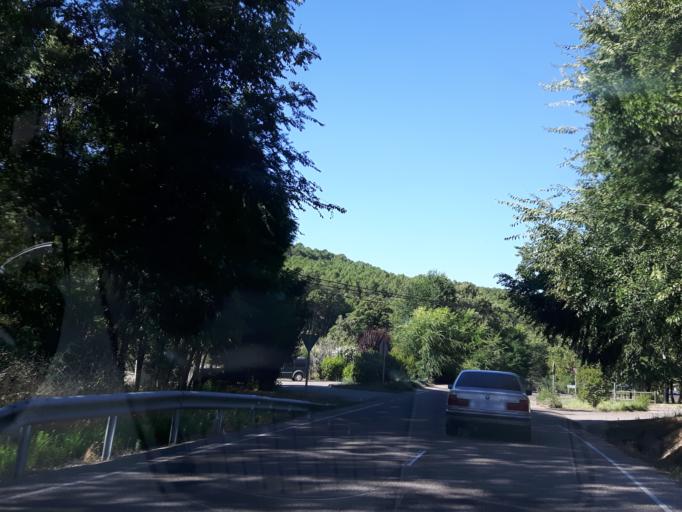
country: ES
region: Castille and Leon
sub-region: Provincia de Avila
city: Arenas de San Pedro
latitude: 40.2219
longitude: -5.0606
